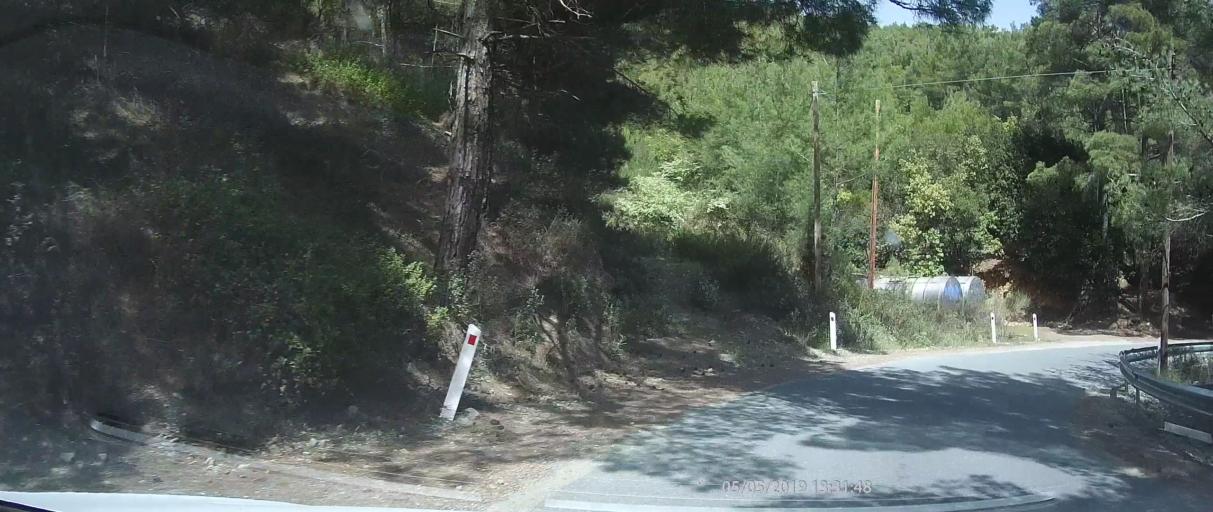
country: CY
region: Lefkosia
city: Kakopetria
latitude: 34.8918
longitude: 32.8514
